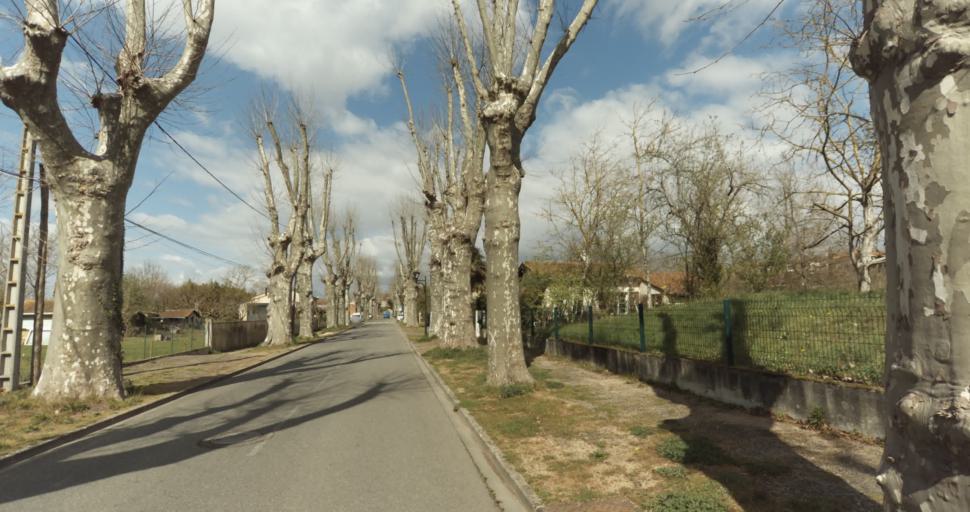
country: FR
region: Midi-Pyrenees
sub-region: Departement de la Haute-Garonne
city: Auterive
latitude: 43.3469
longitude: 1.4790
